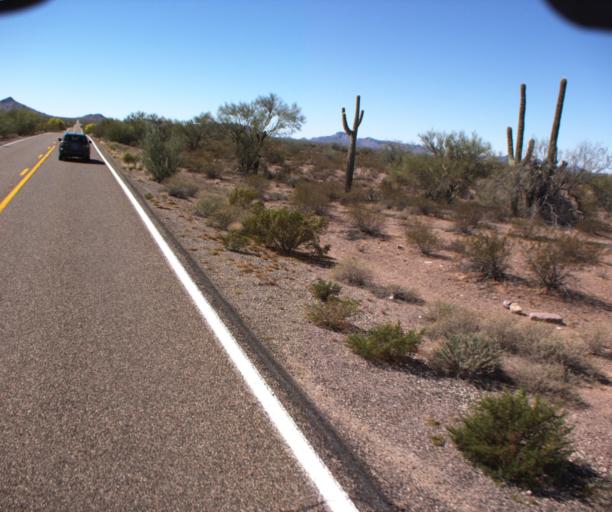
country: US
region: Arizona
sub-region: Pima County
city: Ajo
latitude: 32.1426
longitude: -112.7662
